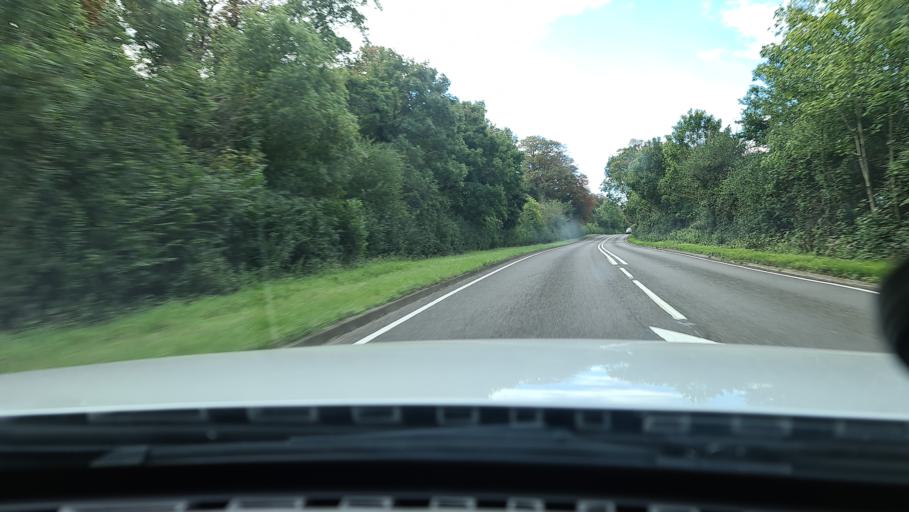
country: GB
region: England
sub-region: Warwickshire
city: Shipston on Stour
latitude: 52.0807
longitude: -1.6232
